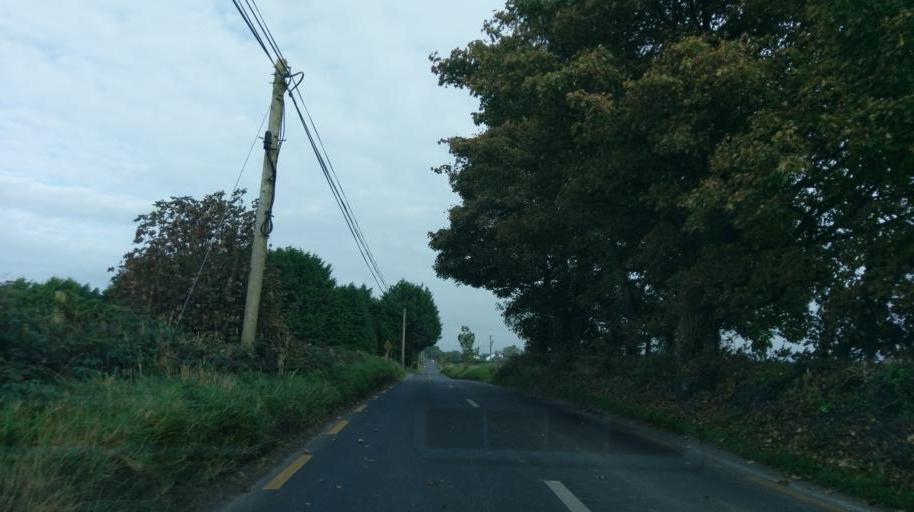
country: IE
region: Connaught
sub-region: County Galway
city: Athenry
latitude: 53.3265
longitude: -8.7250
